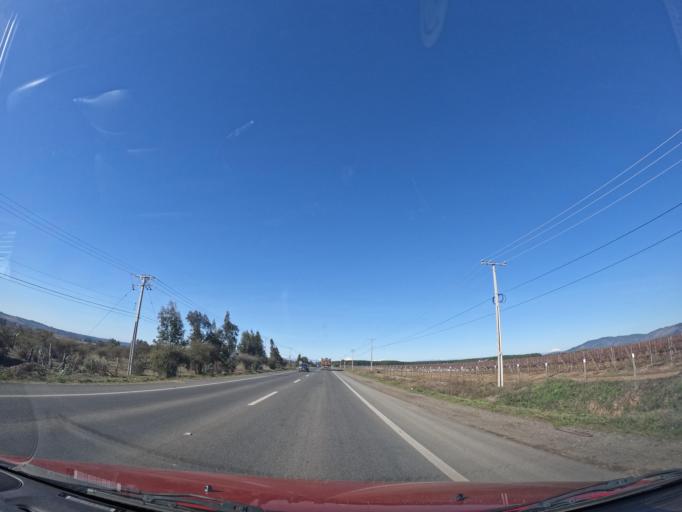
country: CL
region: Maule
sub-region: Provincia de Cauquenes
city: Cauquenes
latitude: -35.9645
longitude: -72.2328
